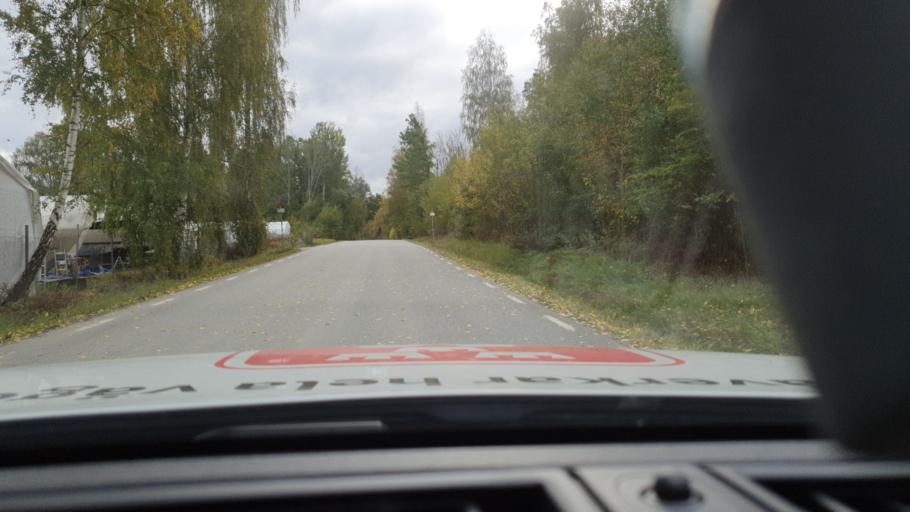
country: SE
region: Stockholm
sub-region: Upplands-Bro Kommun
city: Bro
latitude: 59.4996
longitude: 17.5670
